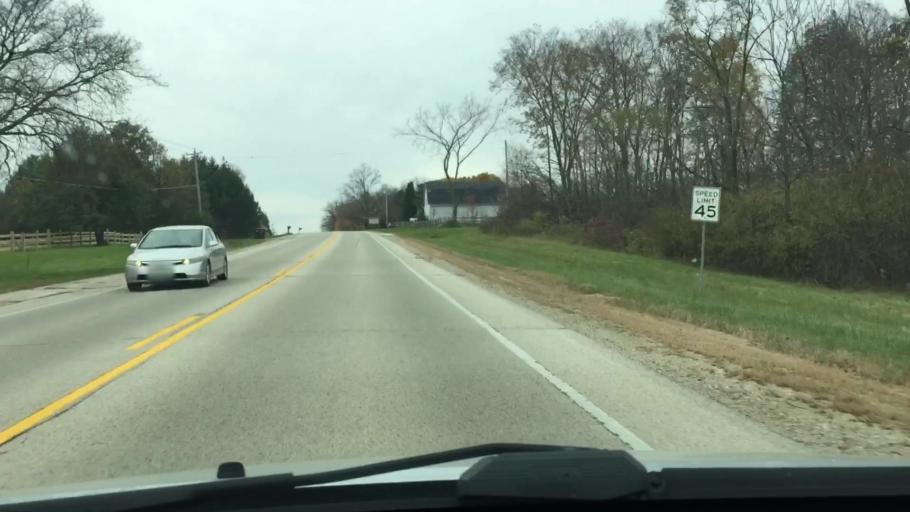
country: US
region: Wisconsin
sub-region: Waukesha County
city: Big Bend
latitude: 42.9081
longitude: -88.2375
